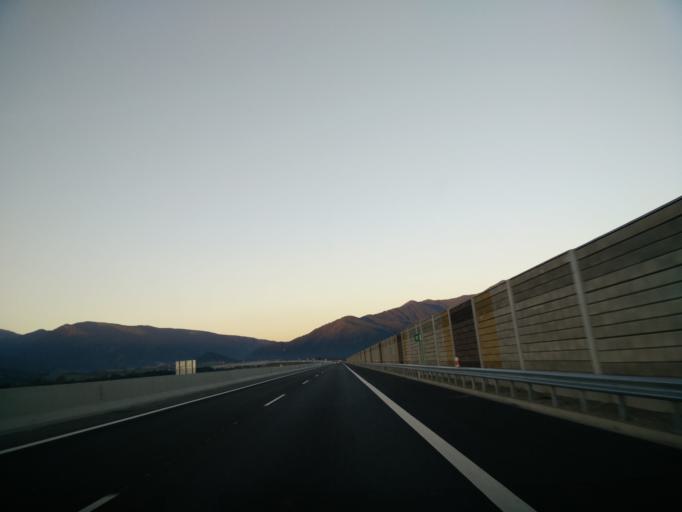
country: SK
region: Zilinsky
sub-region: Okres Martin
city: Martin
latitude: 49.1095
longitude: 19.0554
